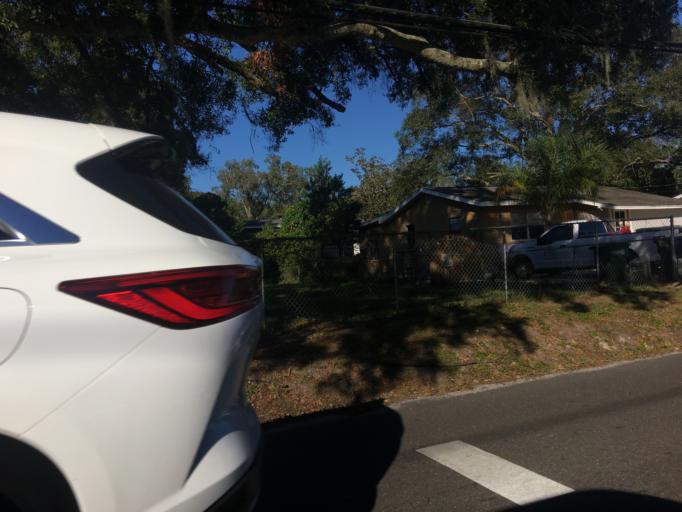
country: US
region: Florida
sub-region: Hillsborough County
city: Egypt Lake-Leto
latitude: 28.0181
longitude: -82.4861
